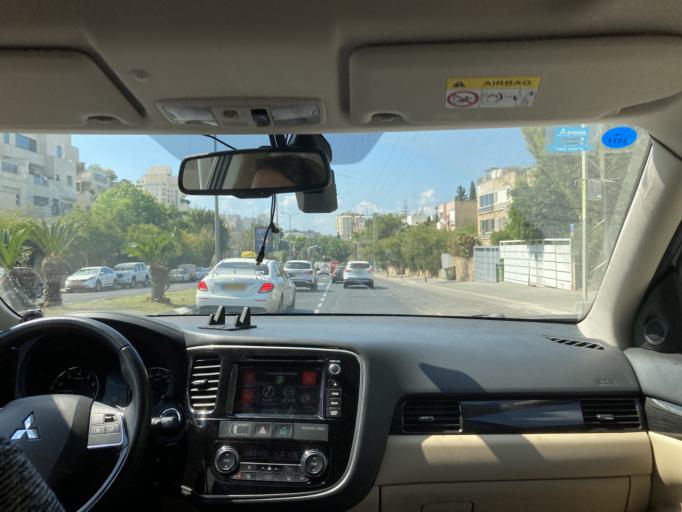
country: IL
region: Tel Aviv
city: Ramat HaSharon
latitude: 32.1186
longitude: 34.8283
